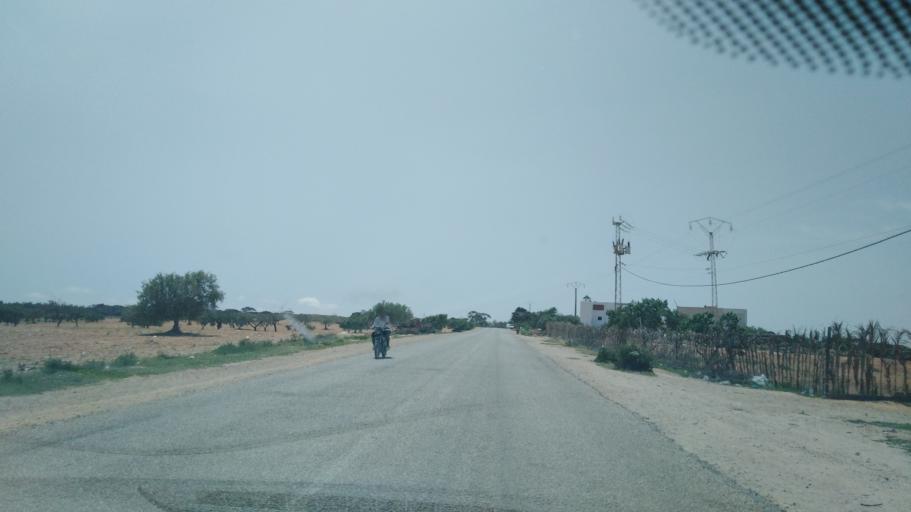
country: TN
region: Safaqis
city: Sfax
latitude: 34.7276
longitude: 10.5765
